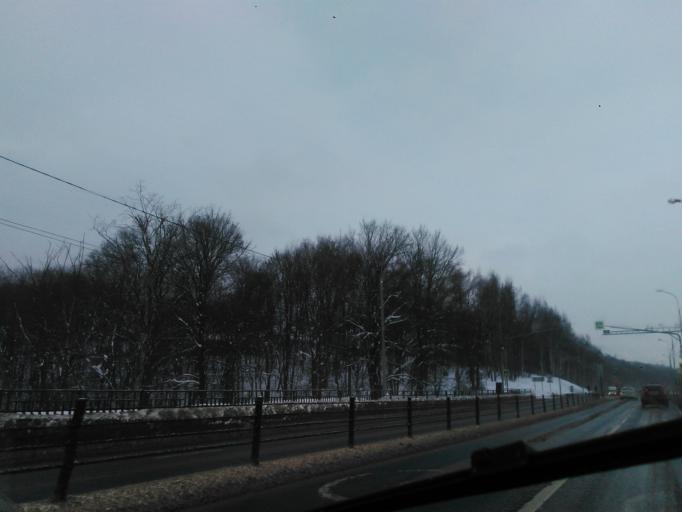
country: RU
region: Moskovskaya
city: Iksha
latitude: 56.1823
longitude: 37.5165
